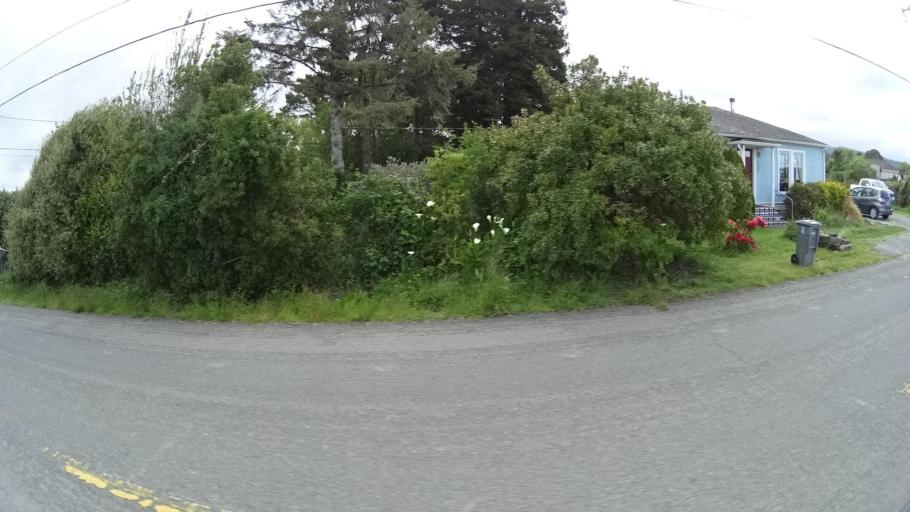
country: US
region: California
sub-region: Humboldt County
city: Arcata
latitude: 40.9041
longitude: -124.0914
